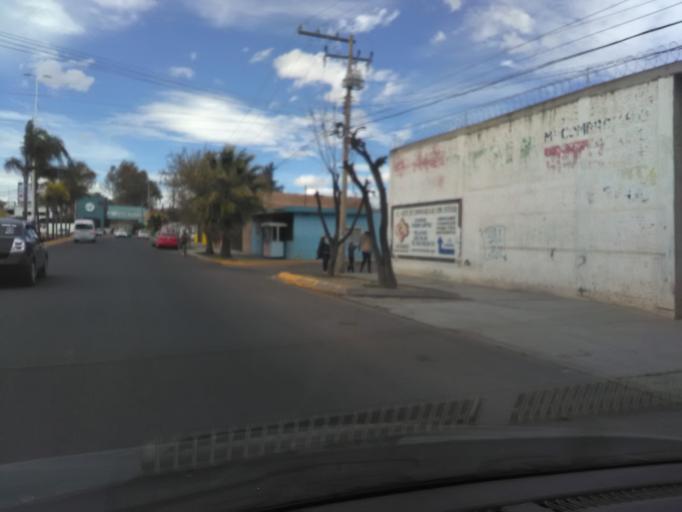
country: MX
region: Durango
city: Victoria de Durango
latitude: 24.0385
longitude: -104.6744
